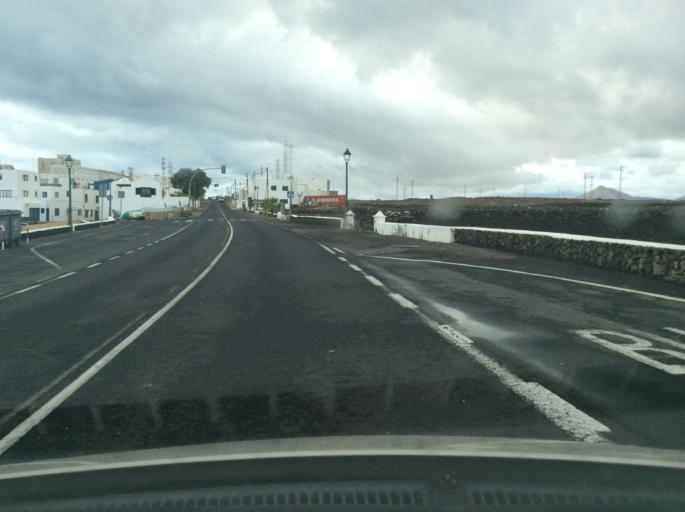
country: ES
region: Canary Islands
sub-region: Provincia de Las Palmas
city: Arrecife
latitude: 28.9819
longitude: -13.5153
